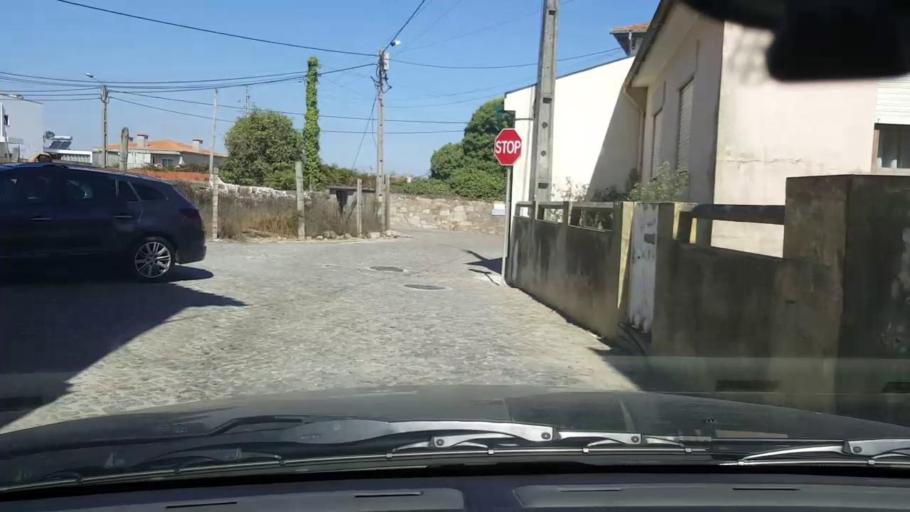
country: PT
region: Porto
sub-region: Matosinhos
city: Lavra
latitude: 41.2662
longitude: -8.6964
